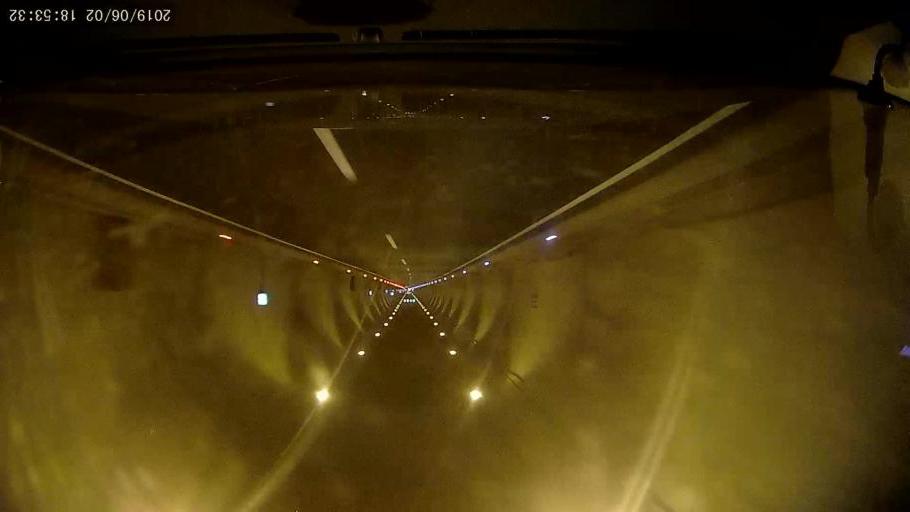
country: TR
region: Ordu
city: Ordu
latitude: 40.9774
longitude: 37.8336
